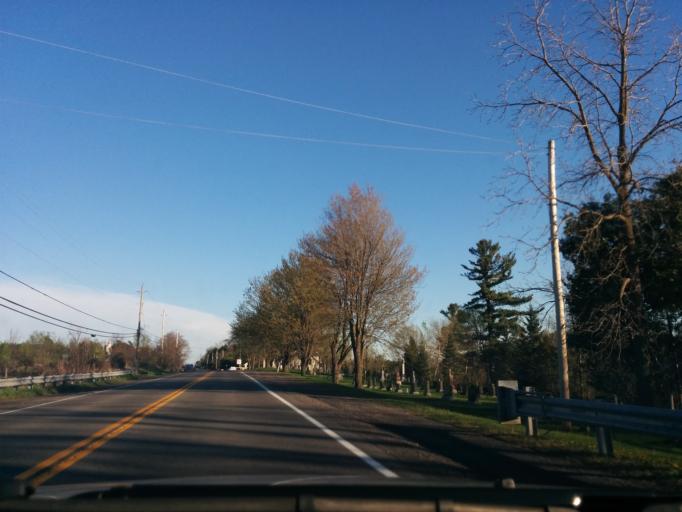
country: CA
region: Ontario
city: Ottawa
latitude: 45.2008
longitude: -75.6387
